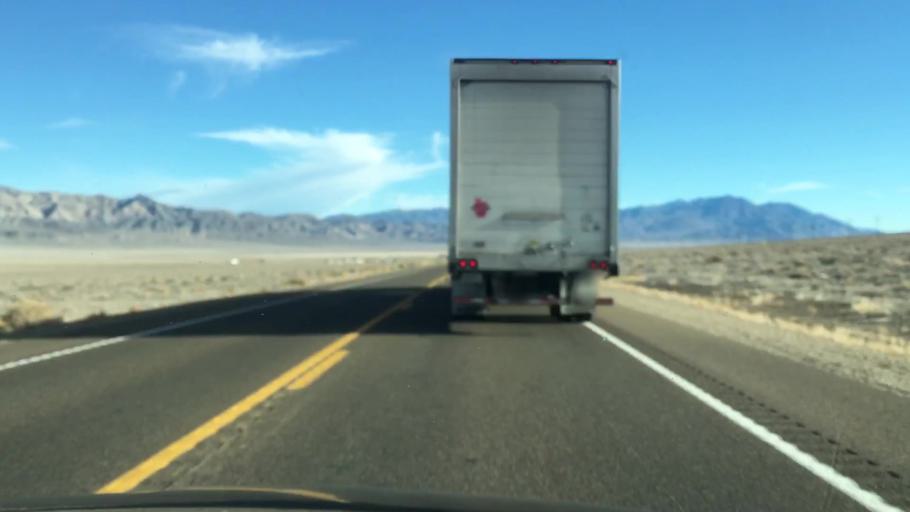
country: US
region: Nevada
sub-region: Mineral County
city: Hawthorne
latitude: 38.5214
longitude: -118.2105
